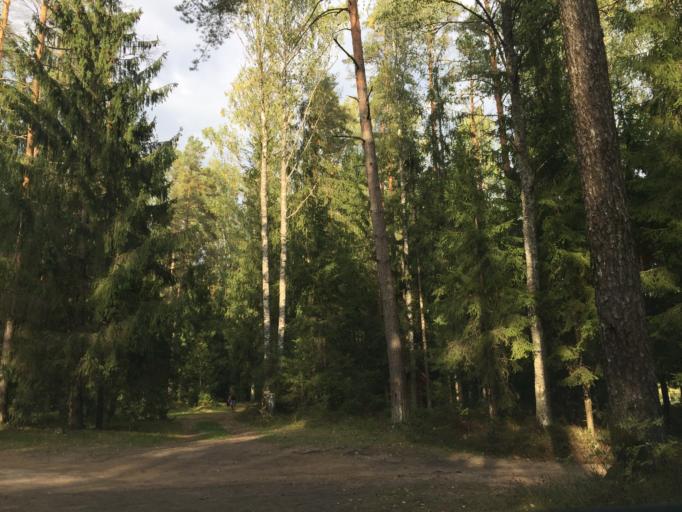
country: LV
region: Baldone
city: Baldone
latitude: 56.7849
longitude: 24.4414
